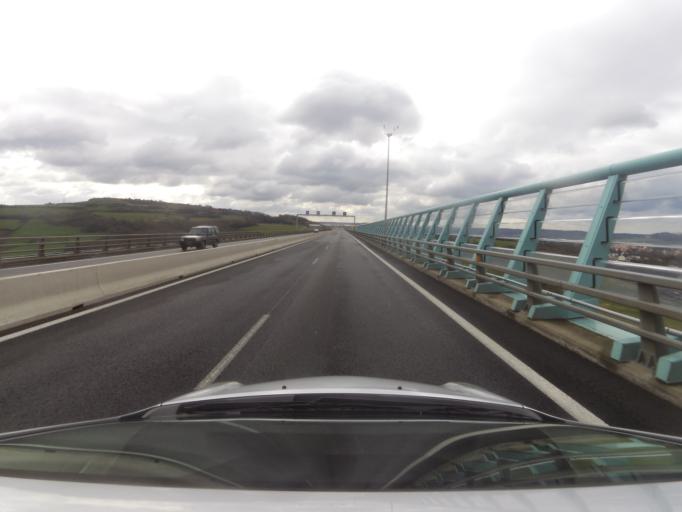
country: FR
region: Nord-Pas-de-Calais
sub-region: Departement du Pas-de-Calais
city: Saint-Leonard
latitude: 50.6976
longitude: 1.6354
